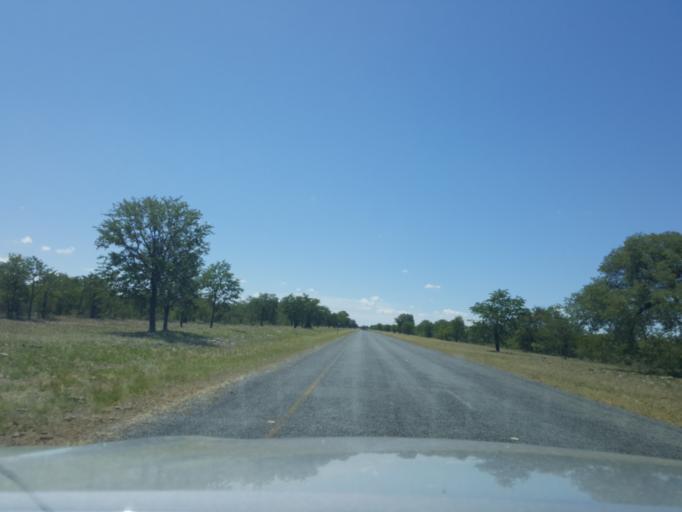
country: BW
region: Central
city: Gweta
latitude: -20.1797
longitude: 25.3293
